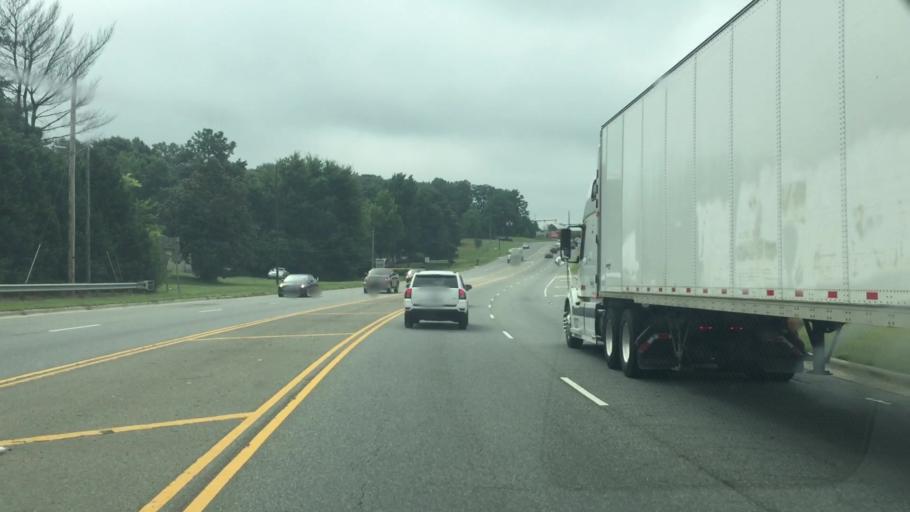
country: US
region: North Carolina
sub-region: Cabarrus County
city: Kannapolis
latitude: 35.4177
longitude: -80.6704
